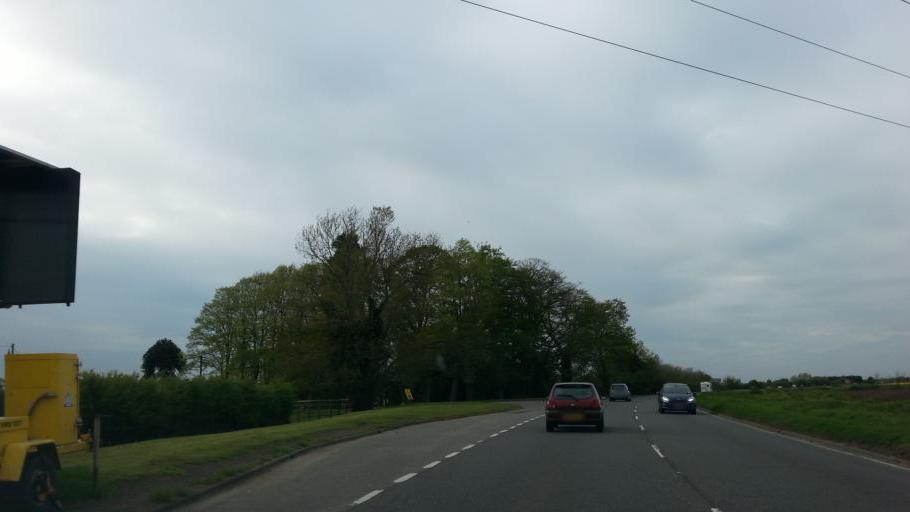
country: GB
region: England
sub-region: Cambridgeshire
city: March
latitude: 52.5746
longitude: 0.0566
